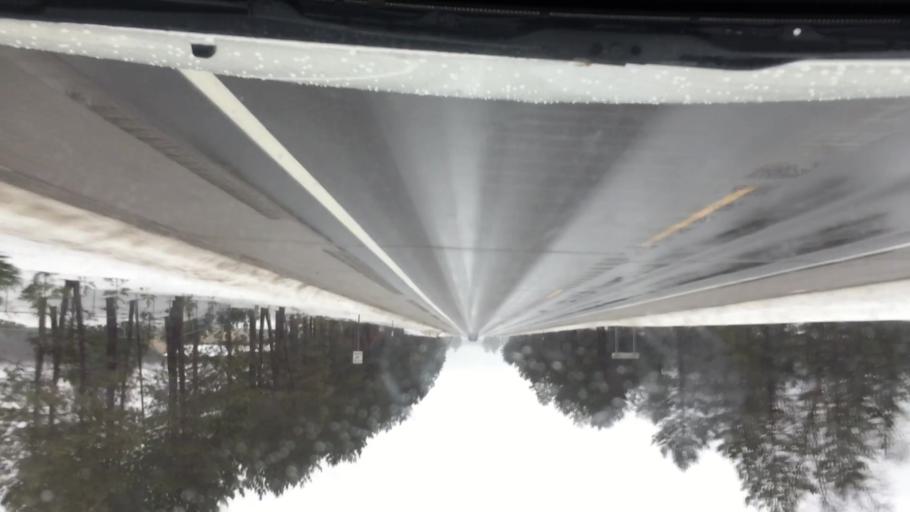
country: US
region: Michigan
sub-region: Kalkaska County
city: Kalkaska
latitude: 44.6843
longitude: -85.2235
